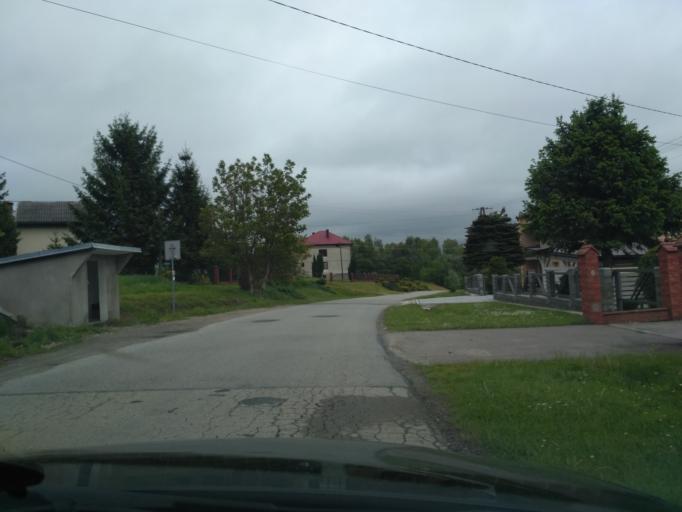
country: PL
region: Subcarpathian Voivodeship
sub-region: Powiat jasielski
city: Brzyska
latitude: 49.8242
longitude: 21.3759
